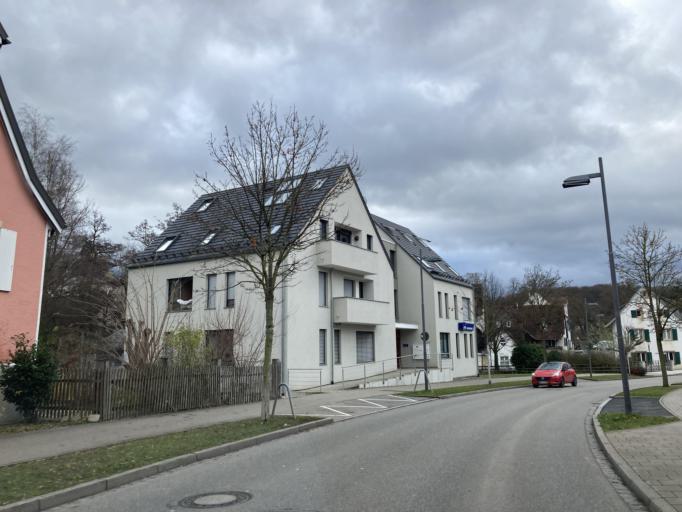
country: DE
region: Baden-Wuerttemberg
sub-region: Freiburg Region
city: Mullheim
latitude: 47.8071
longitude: 7.6315
